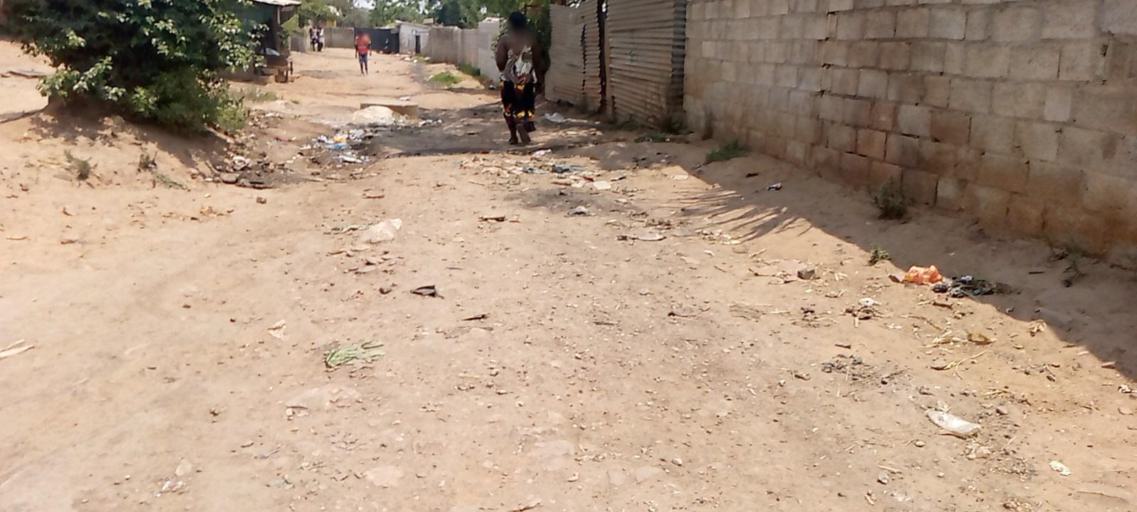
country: ZM
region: Lusaka
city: Lusaka
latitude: -15.3990
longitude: 28.3490
